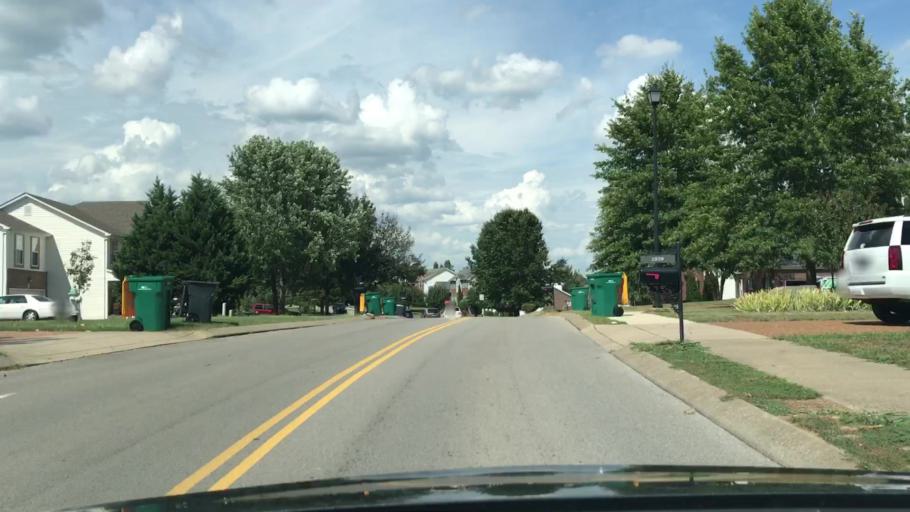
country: US
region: Tennessee
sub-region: Maury County
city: Spring Hill
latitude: 35.7489
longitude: -86.8836
